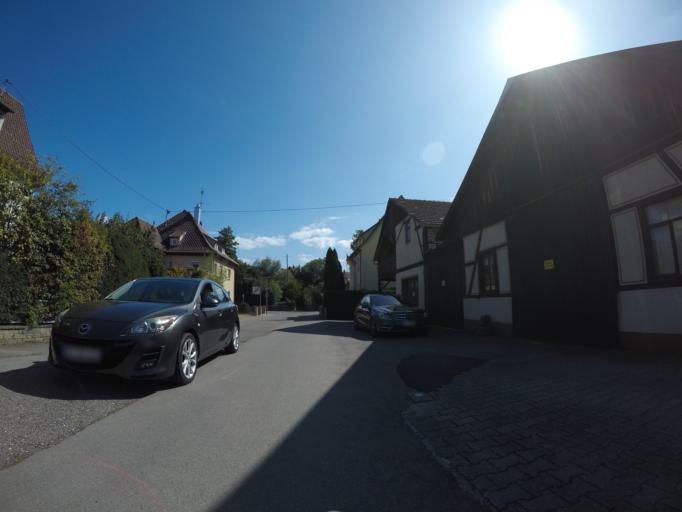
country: DE
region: Baden-Wuerttemberg
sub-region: Tuebingen Region
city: Wannweil
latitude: 48.4967
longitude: 9.1732
